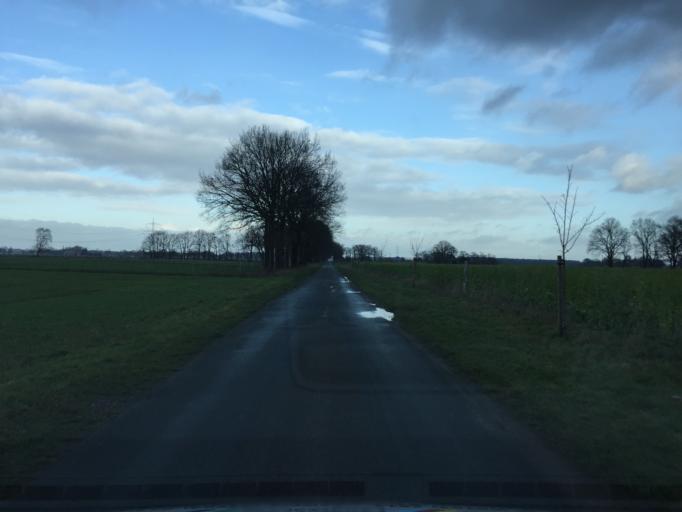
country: DE
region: Lower Saxony
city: Steyerberg
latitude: 52.5233
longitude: 9.0007
